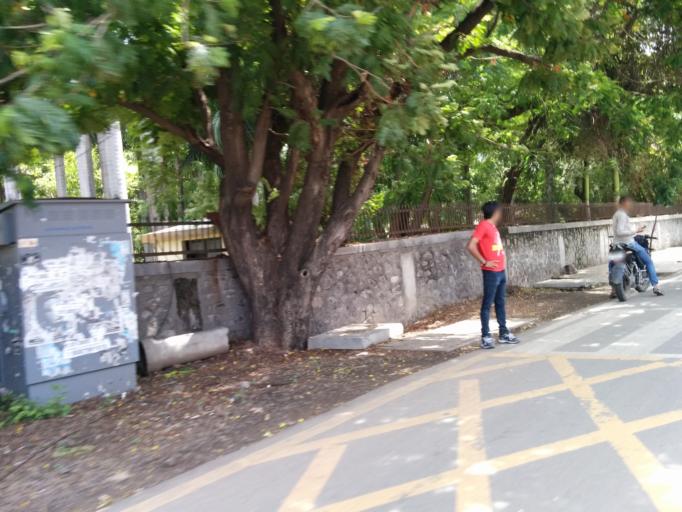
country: IN
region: Maharashtra
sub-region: Pune Division
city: Pune
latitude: 18.5325
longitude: 73.9173
